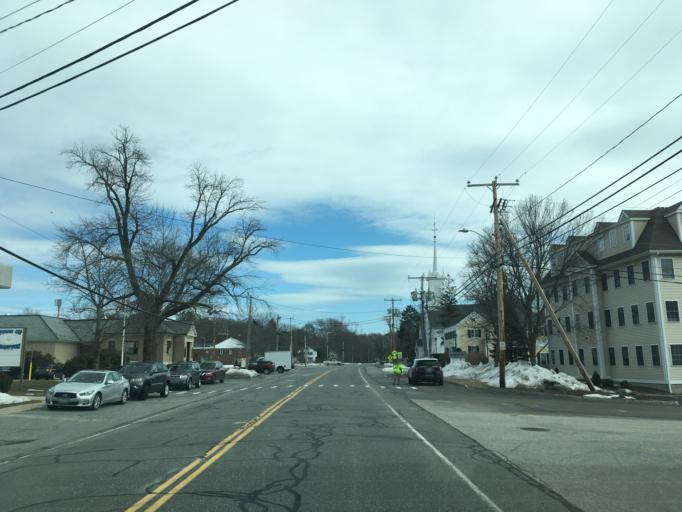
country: US
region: New Hampshire
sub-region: Rockingham County
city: Hampton
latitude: 42.9376
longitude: -70.8349
